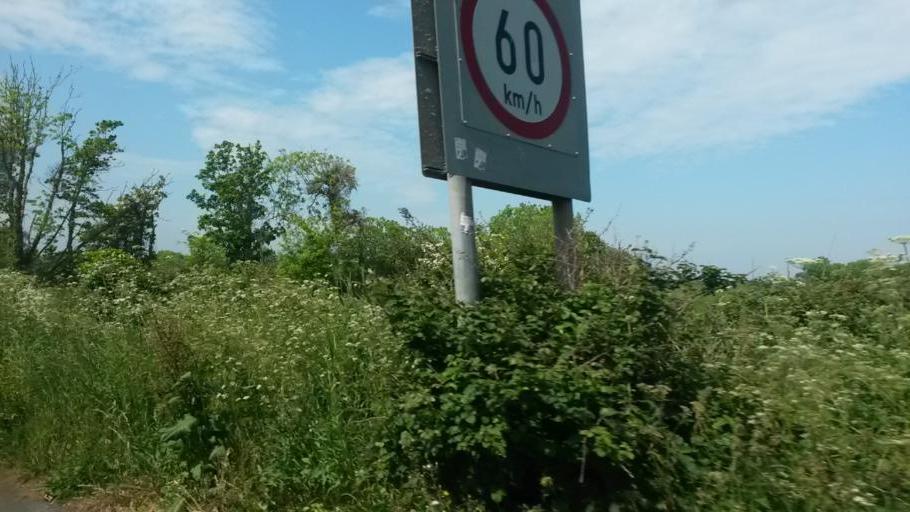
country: IE
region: Leinster
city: Portraine
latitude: 53.4938
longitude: -6.1186
